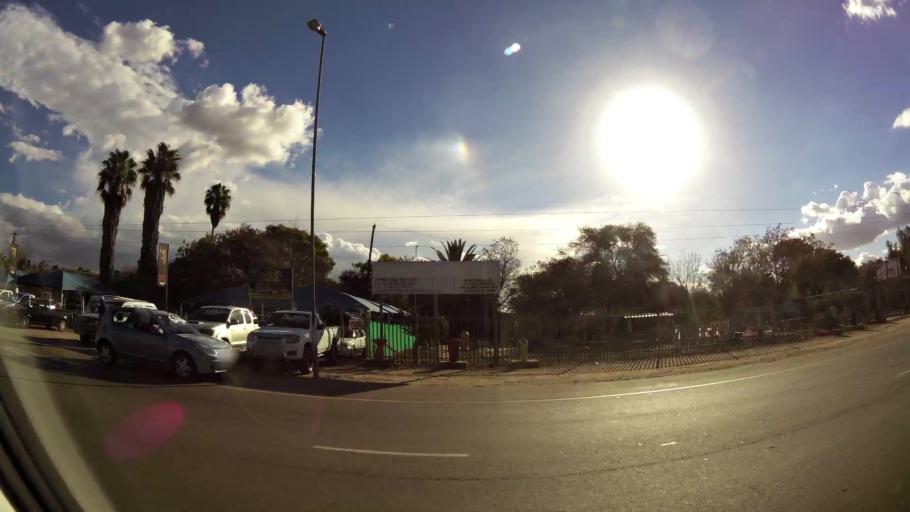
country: ZA
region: Limpopo
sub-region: Capricorn District Municipality
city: Polokwane
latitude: -23.9294
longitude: 29.4506
